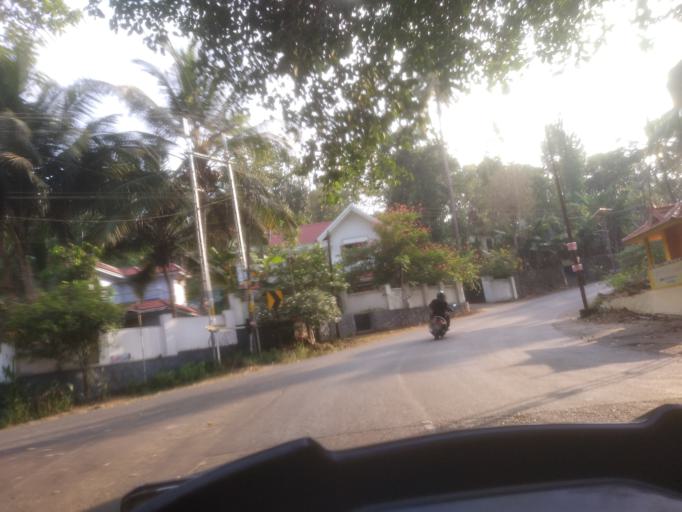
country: IN
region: Kerala
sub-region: Ernakulam
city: Piravam
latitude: 9.8124
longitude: 76.4985
